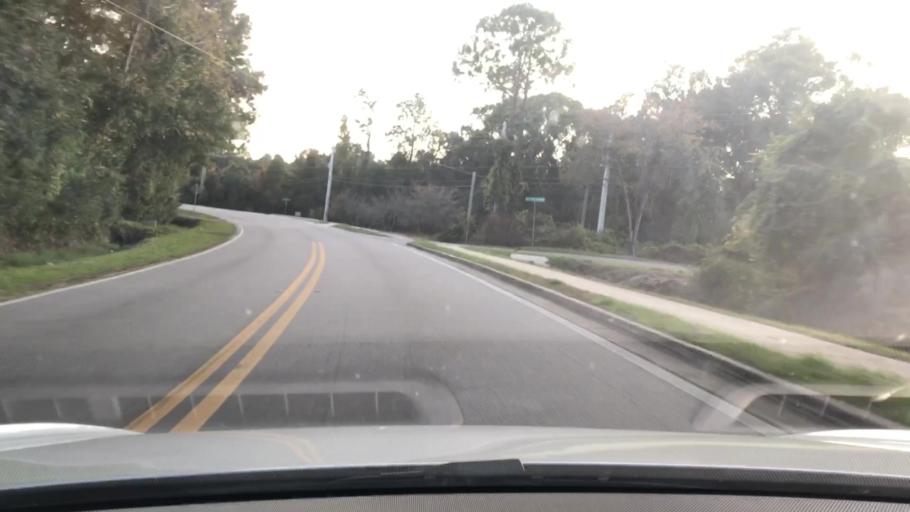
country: US
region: Florida
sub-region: Saint Johns County
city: Villano Beach
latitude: 29.9372
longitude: -81.3448
